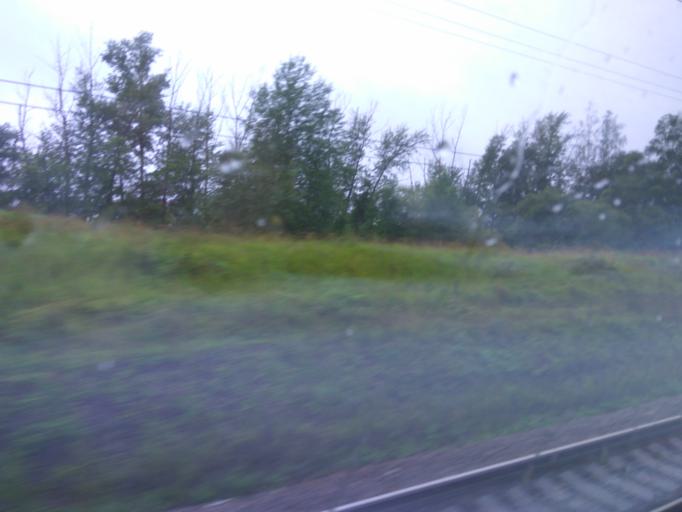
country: RU
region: Moskovskaya
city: Stupino
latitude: 54.9013
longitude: 38.0862
